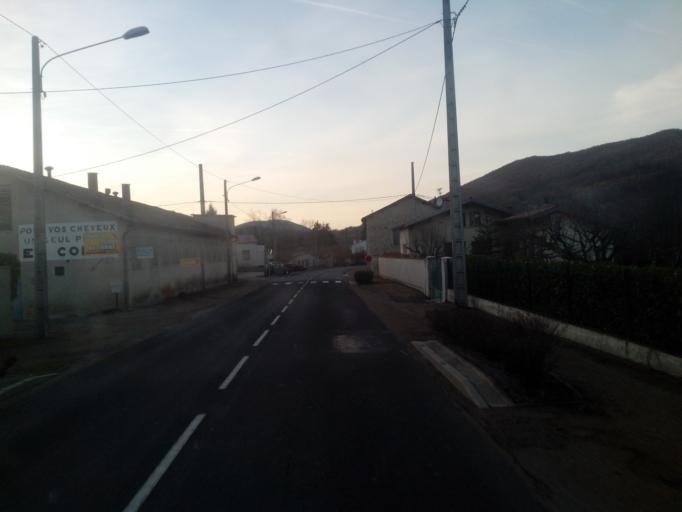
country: FR
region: Midi-Pyrenees
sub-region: Departement de l'Ariege
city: Belesta
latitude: 42.9155
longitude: 1.9053
